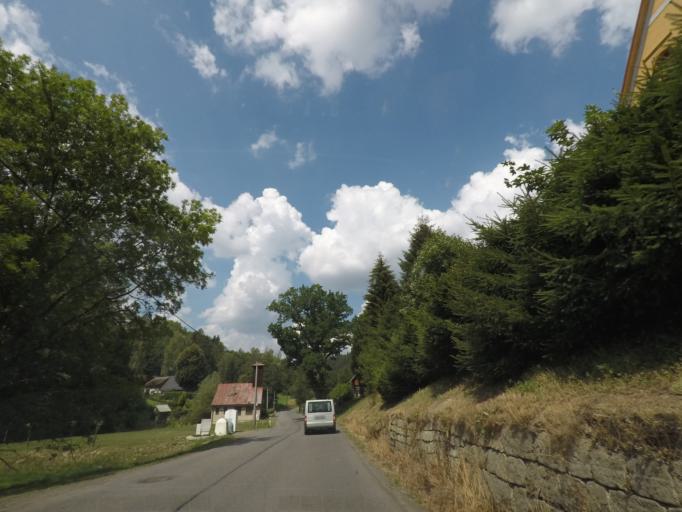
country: CZ
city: Radvanice
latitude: 50.6195
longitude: 16.1053
